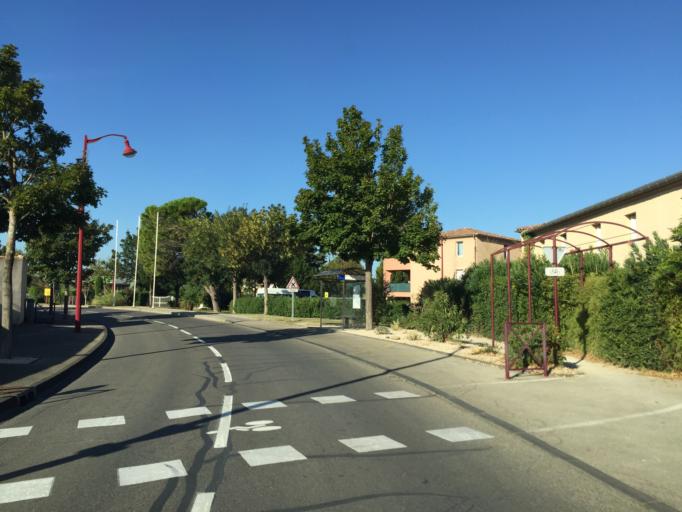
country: FR
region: Provence-Alpes-Cote d'Azur
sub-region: Departement du Vaucluse
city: Entraigues-sur-la-Sorgue
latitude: 44.0014
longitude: 4.9213
